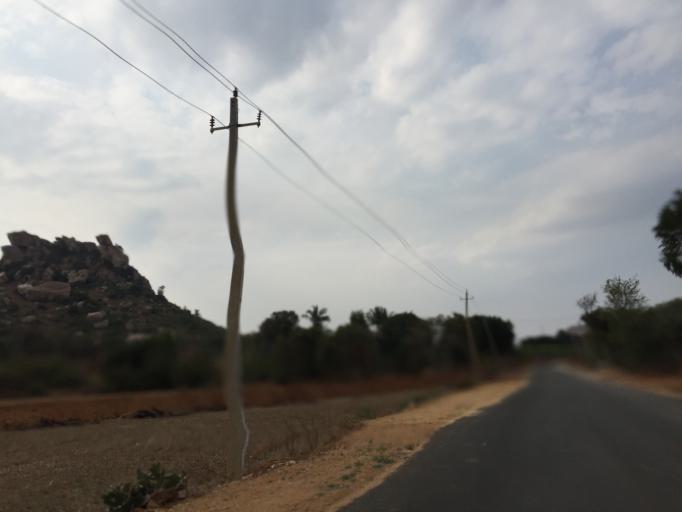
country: IN
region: Karnataka
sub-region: Chikkaballapur
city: Gudibanda
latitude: 13.5613
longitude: 77.7371
